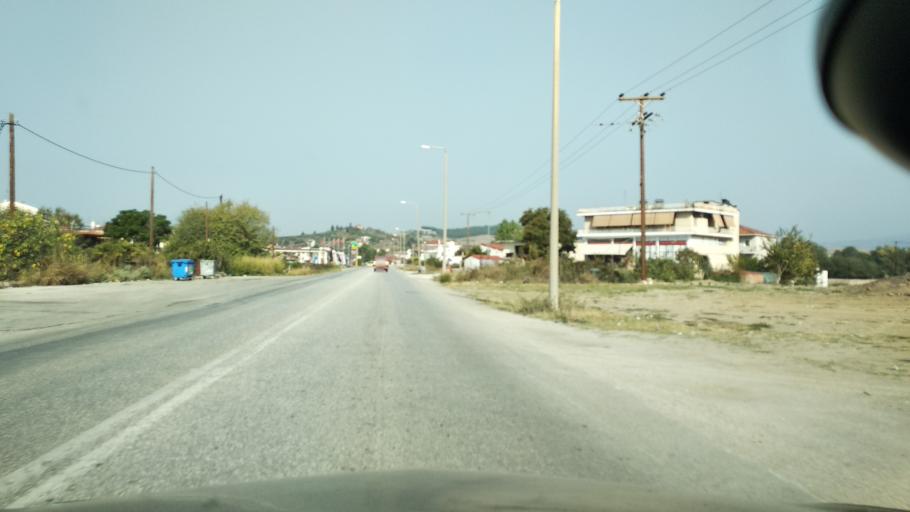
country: GR
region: Thessaly
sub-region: Trikala
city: Trikala
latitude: 39.5611
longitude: 21.7826
